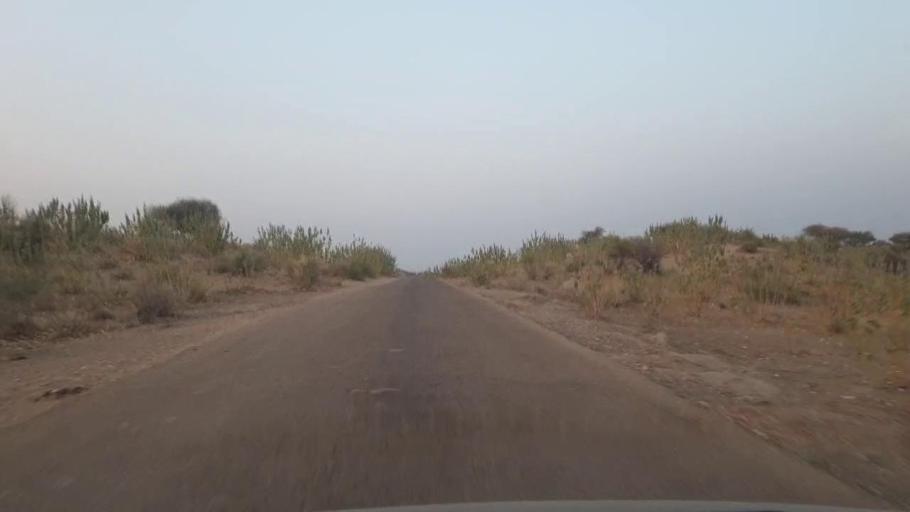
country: PK
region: Sindh
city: Umarkot
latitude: 25.3311
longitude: 70.0577
